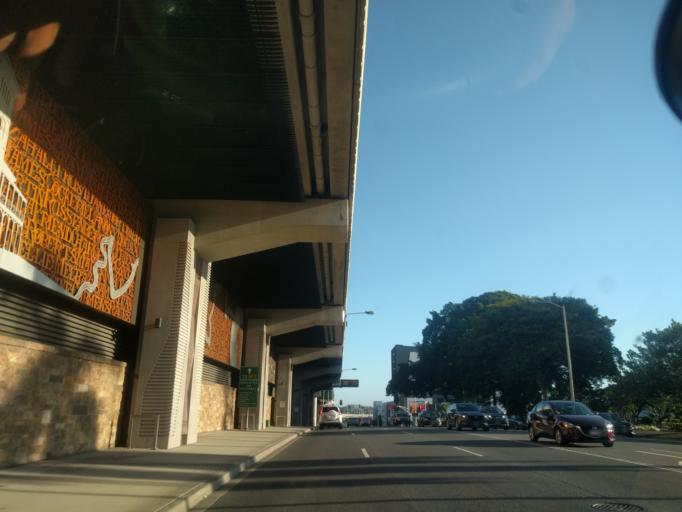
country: AU
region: Queensland
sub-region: Brisbane
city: Fortitude Valley
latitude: -27.4492
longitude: 153.0290
